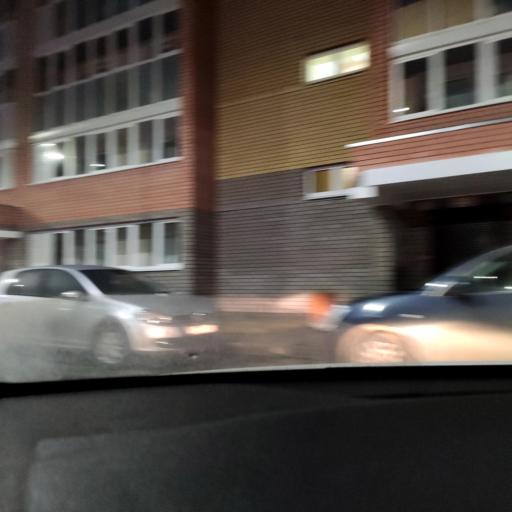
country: RU
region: Tatarstan
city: Osinovo
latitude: 55.8692
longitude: 48.8779
